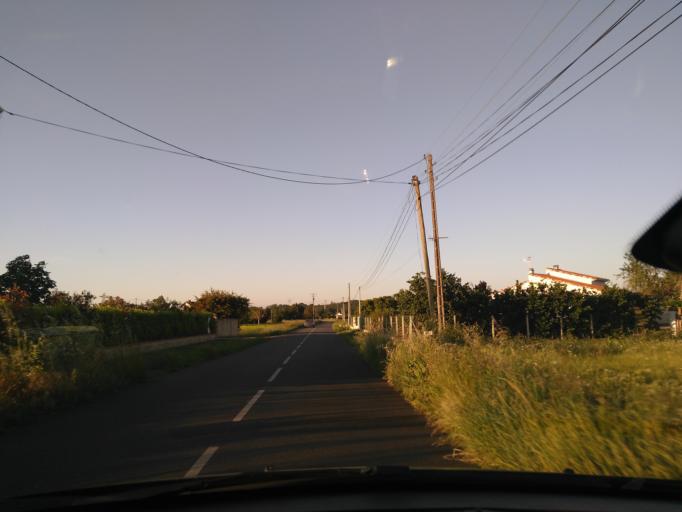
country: FR
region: Midi-Pyrenees
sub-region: Departement de la Haute-Garonne
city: Grenade
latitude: 43.7476
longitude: 1.2852
